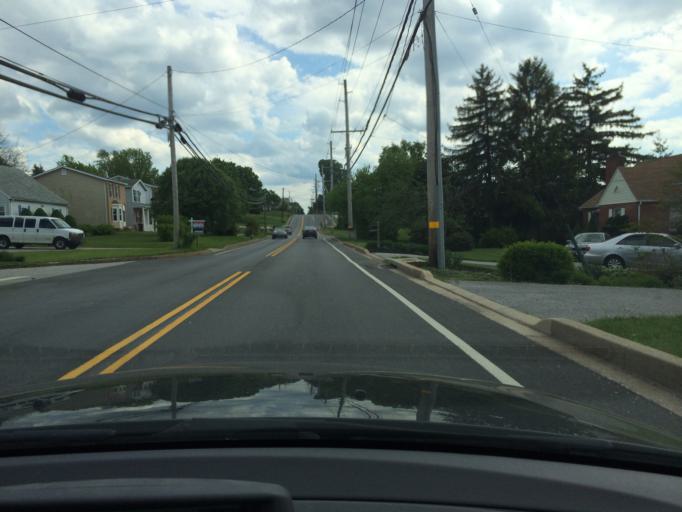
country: US
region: Maryland
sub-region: Carroll County
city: Westminster
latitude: 39.5528
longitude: -76.9901
